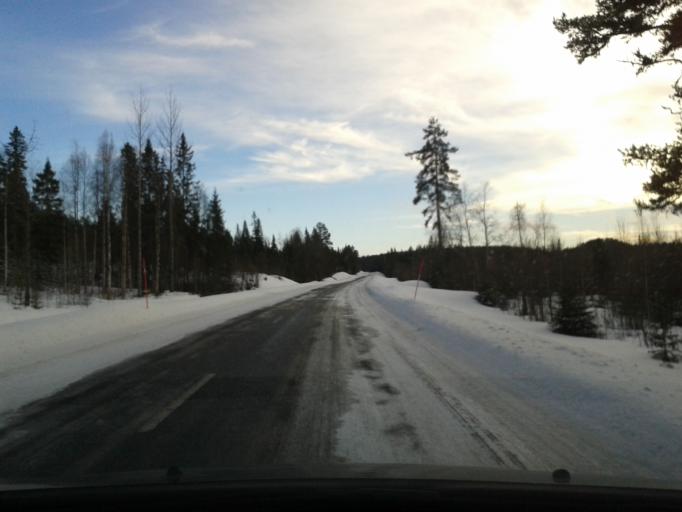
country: SE
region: Vaesterbotten
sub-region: Asele Kommun
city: Asele
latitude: 64.2216
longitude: 17.3074
